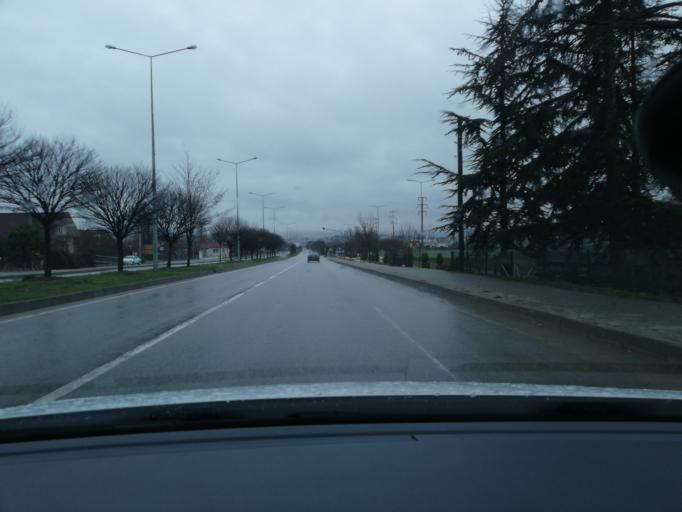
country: TR
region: Bolu
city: Bolu
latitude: 40.7127
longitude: 31.6157
